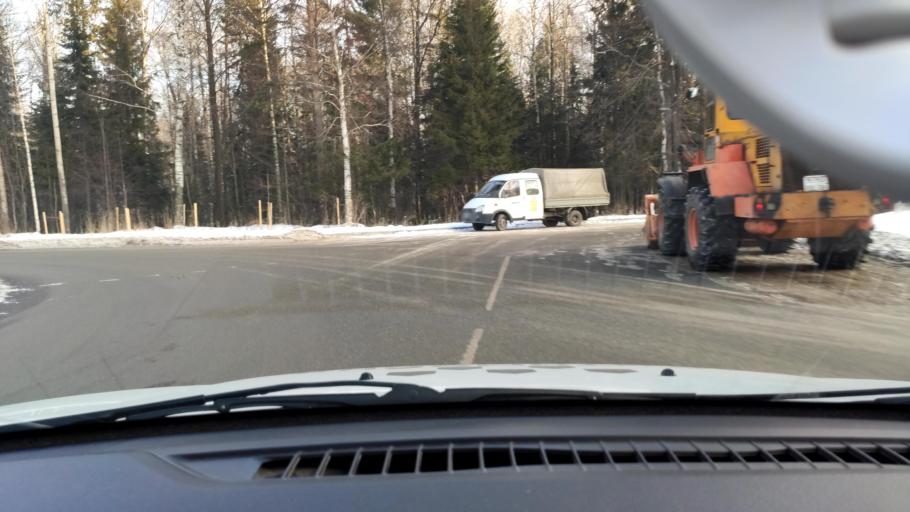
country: RU
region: Perm
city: Perm
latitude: 58.0860
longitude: 56.4132
